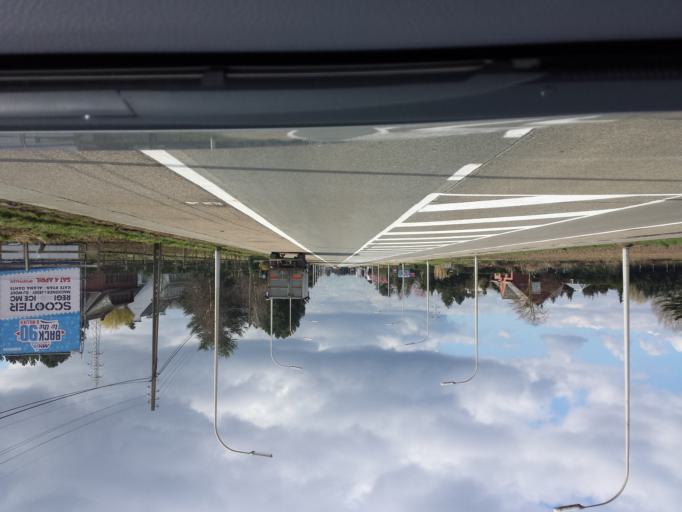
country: BE
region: Flanders
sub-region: Provincie Limburg
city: Halen
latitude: 50.9588
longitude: 5.0892
